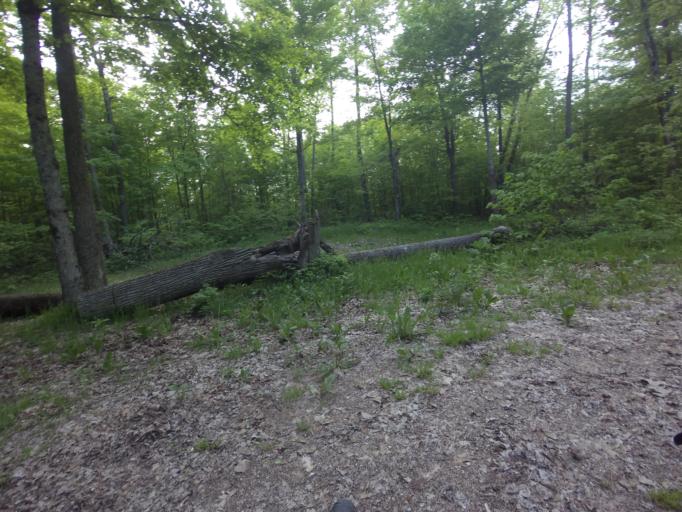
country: US
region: New York
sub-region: St. Lawrence County
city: Gouverneur
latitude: 44.1621
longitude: -75.3888
